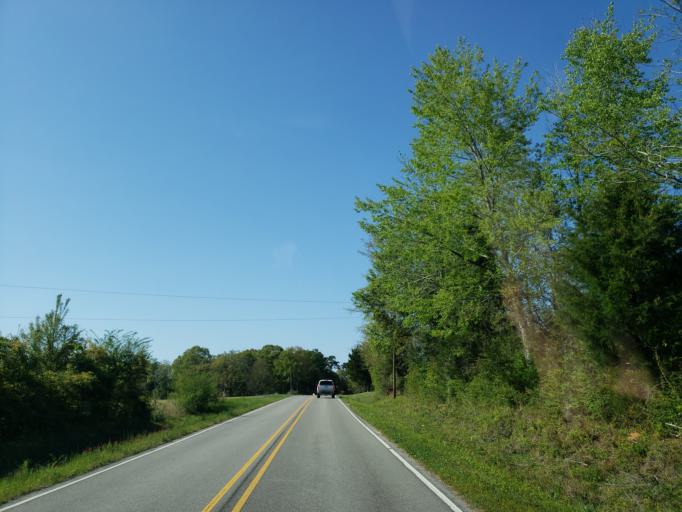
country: US
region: Mississippi
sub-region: Covington County
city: Collins
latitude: 31.6176
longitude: -89.3893
